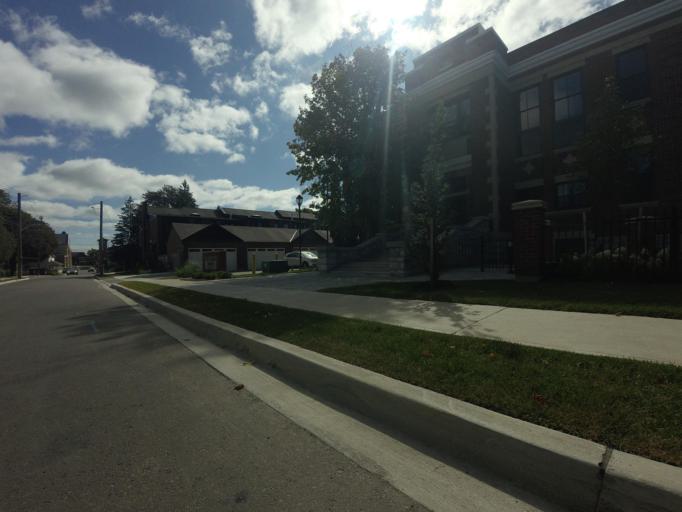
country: CA
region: Ontario
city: Newmarket
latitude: 44.0532
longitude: -79.4608
